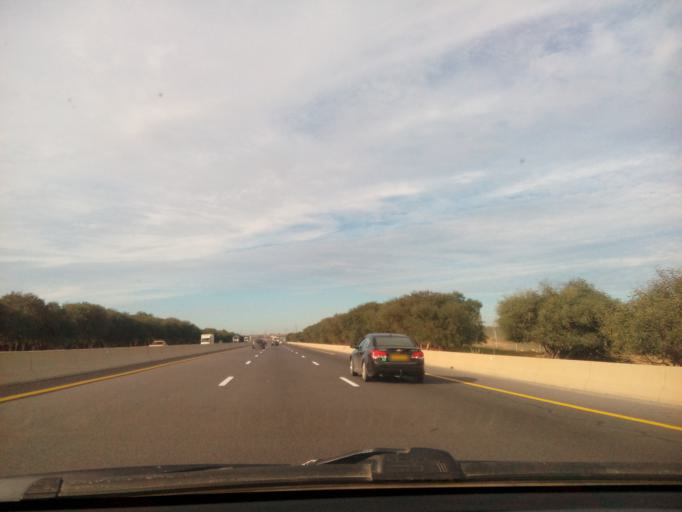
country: DZ
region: Mascara
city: Sig
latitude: 35.5420
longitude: -0.3588
